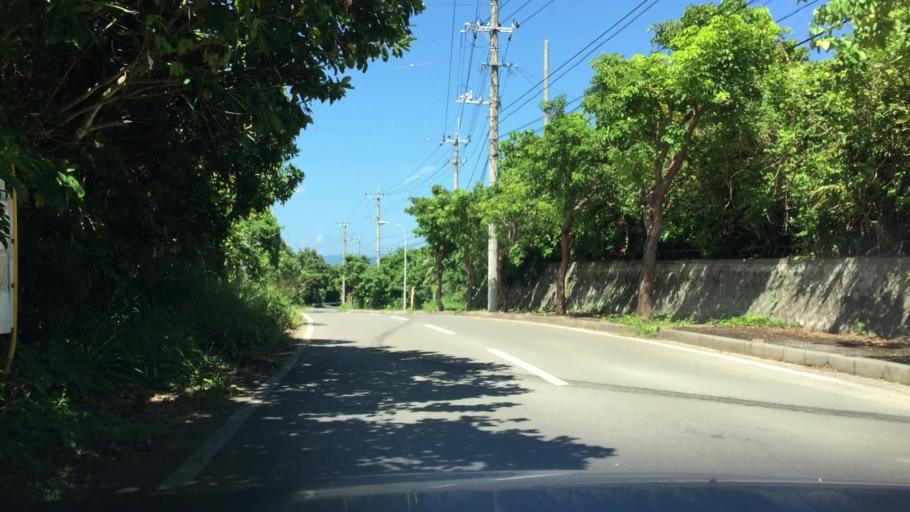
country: JP
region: Okinawa
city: Ishigaki
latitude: 24.4478
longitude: 124.1810
